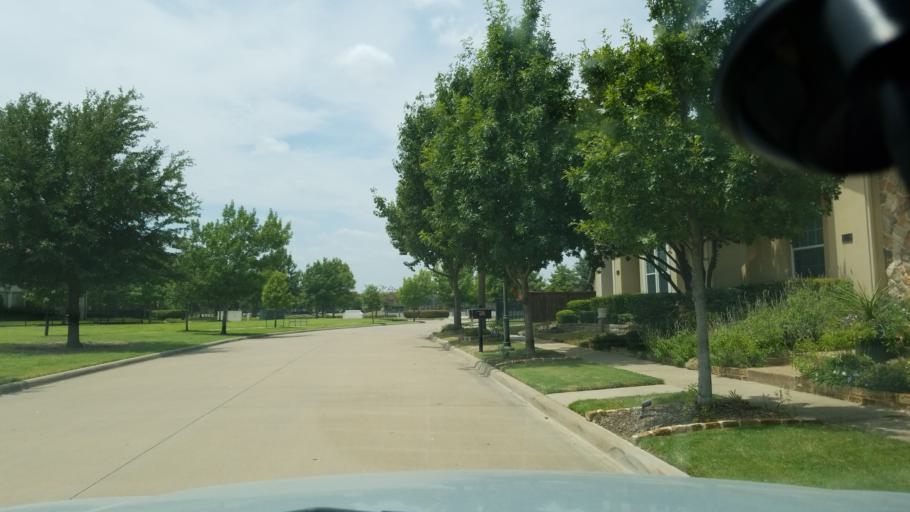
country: US
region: Texas
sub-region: Dallas County
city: Farmers Branch
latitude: 32.8987
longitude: -96.9302
